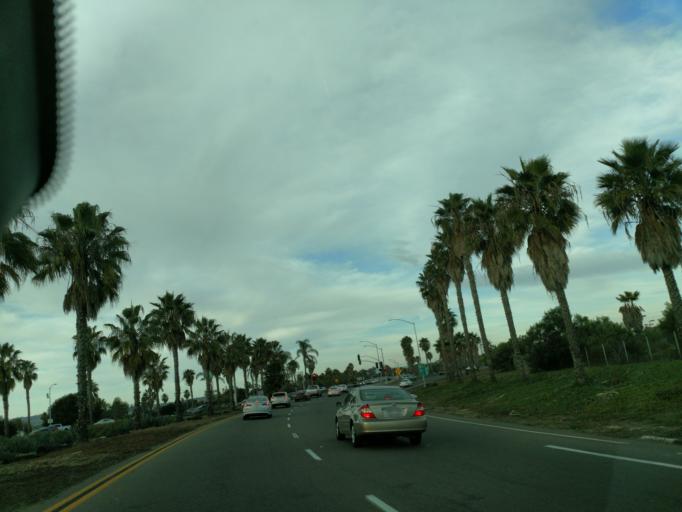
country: US
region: California
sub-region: San Diego County
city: Coronado
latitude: 32.7535
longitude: -117.2367
